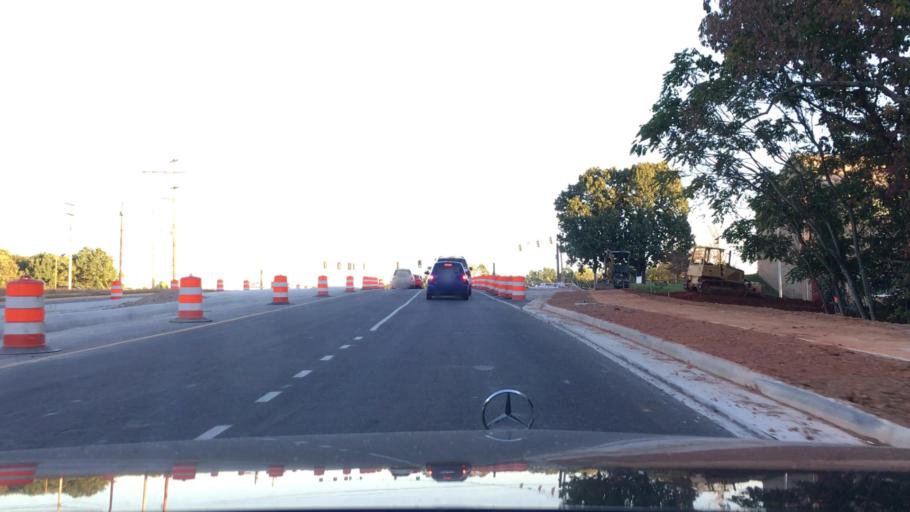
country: US
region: Virginia
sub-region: Campbell County
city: Timberlake
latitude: 37.3347
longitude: -79.2162
